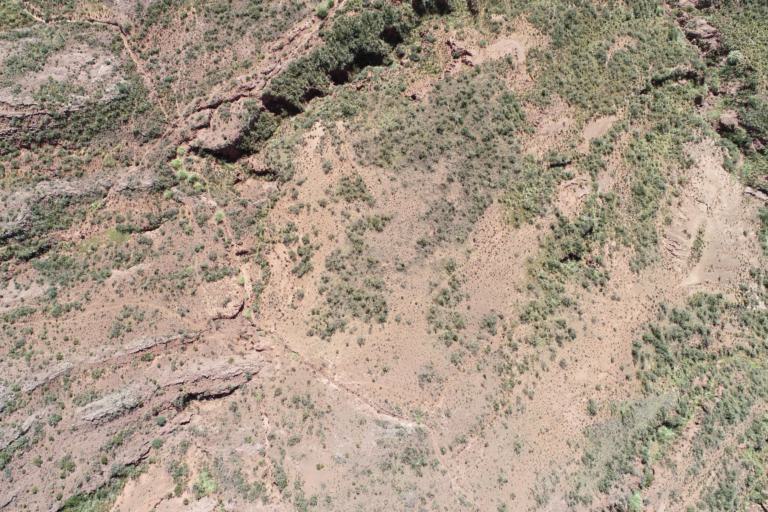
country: BO
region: La Paz
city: Tiahuanaco
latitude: -16.5988
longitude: -68.7557
